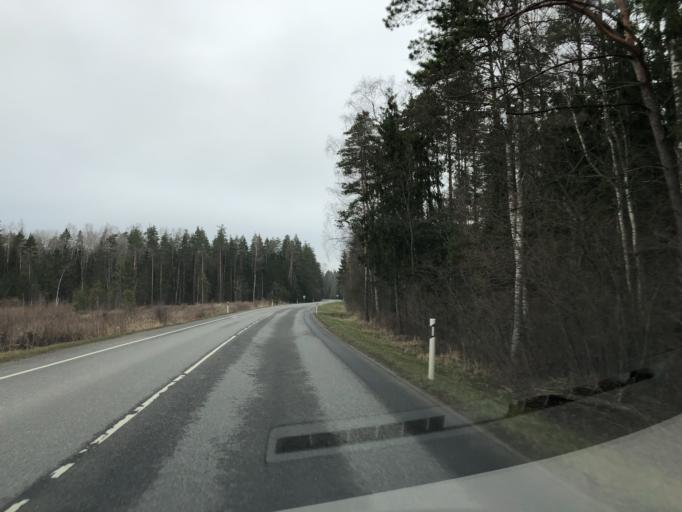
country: EE
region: Laeaene-Virumaa
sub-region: Vaeike-Maarja vald
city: Vaike-Maarja
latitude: 59.0702
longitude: 26.2379
